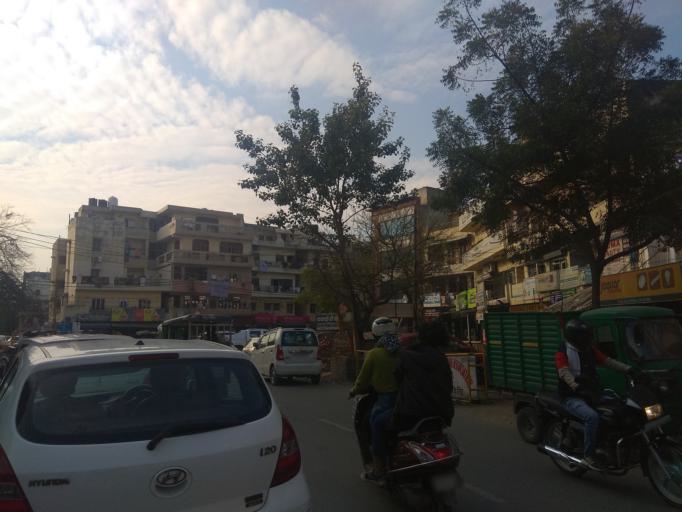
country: IN
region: NCT
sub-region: West Delhi
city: Nangloi Jat
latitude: 28.6365
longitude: 77.0683
